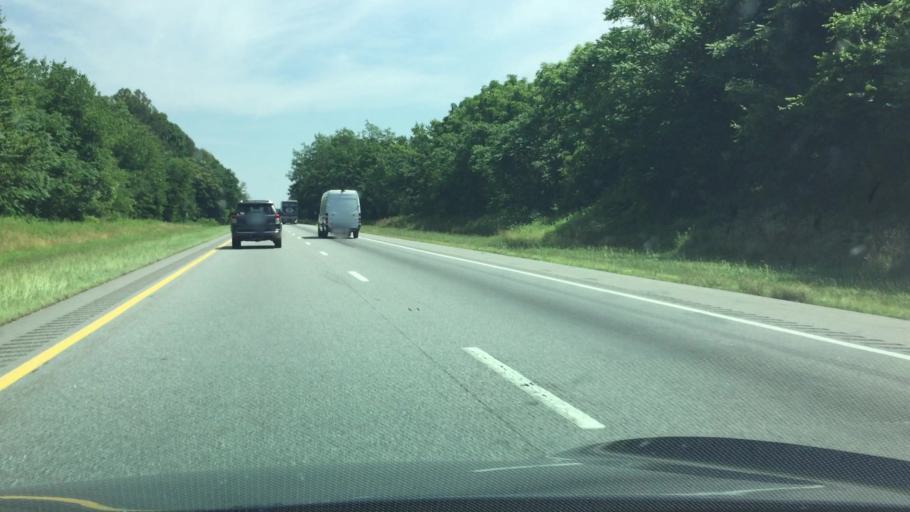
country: US
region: North Carolina
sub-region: Yadkin County
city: Jonesville
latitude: 36.0777
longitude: -80.8196
